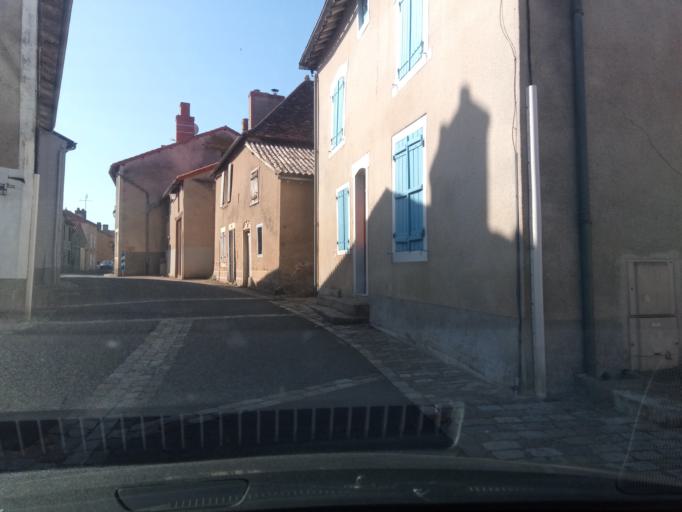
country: FR
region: Poitou-Charentes
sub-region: Departement de la Vienne
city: Saulge
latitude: 46.3329
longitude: 0.8726
